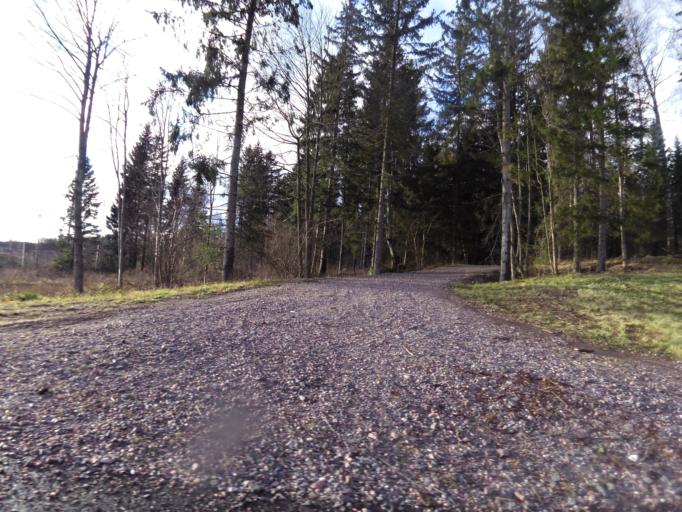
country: FI
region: Uusimaa
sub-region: Helsinki
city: Kilo
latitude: 60.2047
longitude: 24.7855
